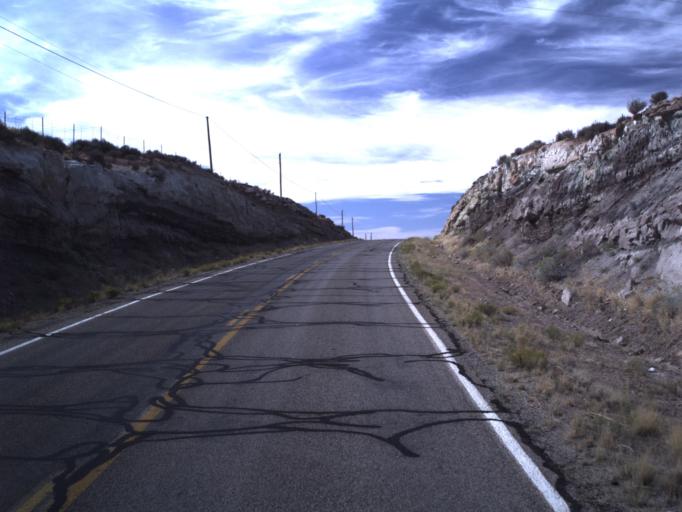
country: US
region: Utah
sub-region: San Juan County
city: Blanding
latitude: 37.2879
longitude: -109.2898
